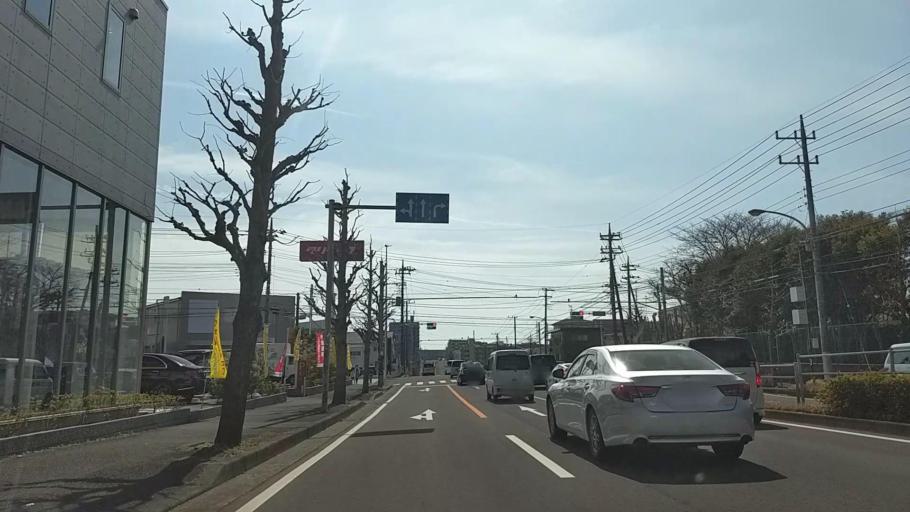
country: JP
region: Kanagawa
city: Fujisawa
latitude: 35.3838
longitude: 139.4565
